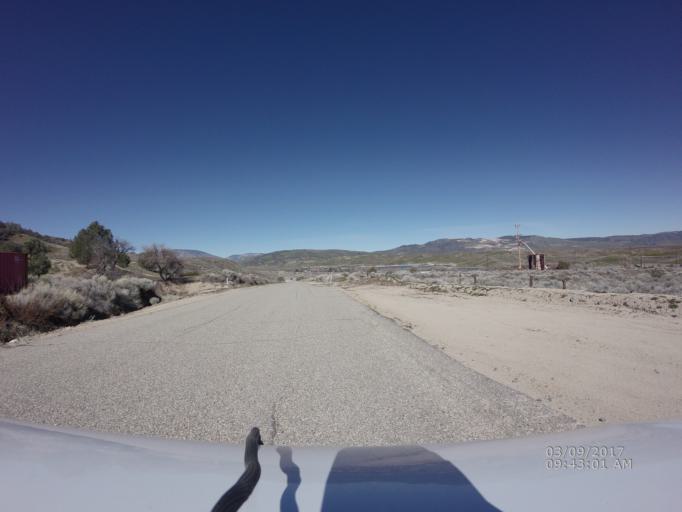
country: US
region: California
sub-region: Kern County
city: Lebec
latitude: 34.7628
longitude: -118.7288
